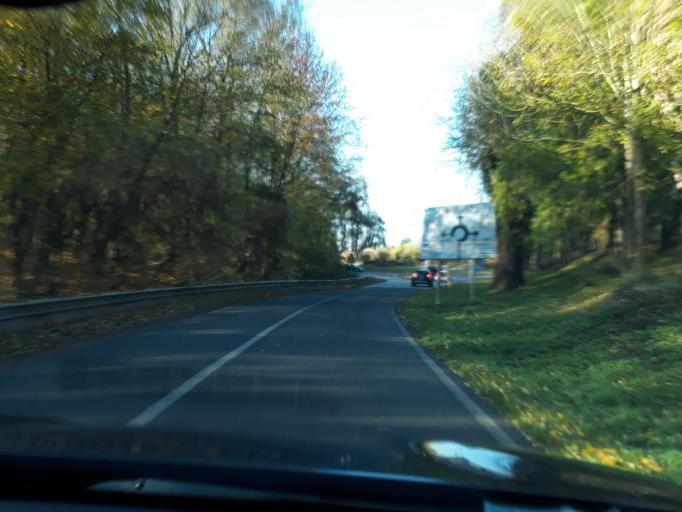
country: FR
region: Nord-Pas-de-Calais
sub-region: Departement du Nord
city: Sin-le-Noble
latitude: 50.3619
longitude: 3.1265
